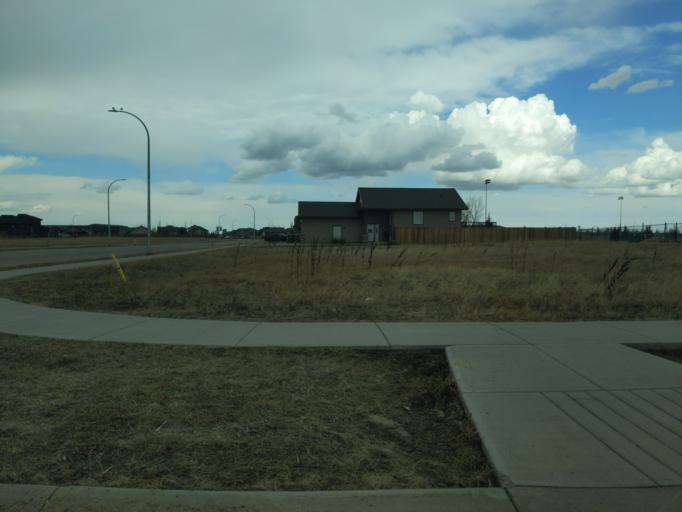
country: CA
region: Saskatchewan
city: Lloydminster
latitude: 53.2691
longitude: -110.0464
